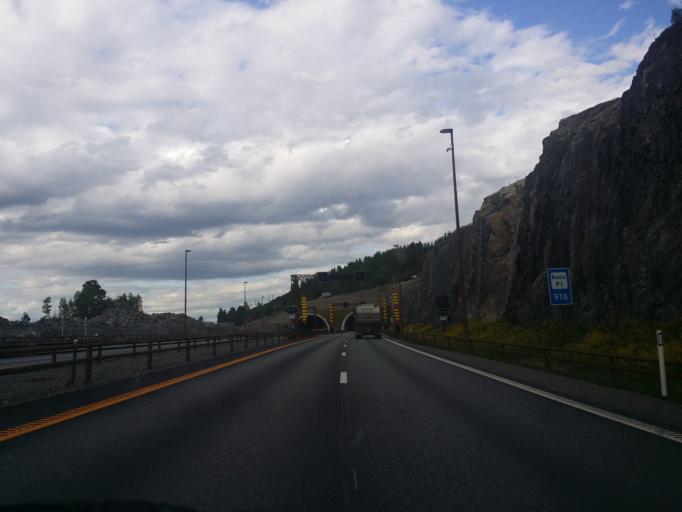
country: NO
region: Hedmark
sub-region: Stange
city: Stange
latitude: 60.5728
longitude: 11.2660
